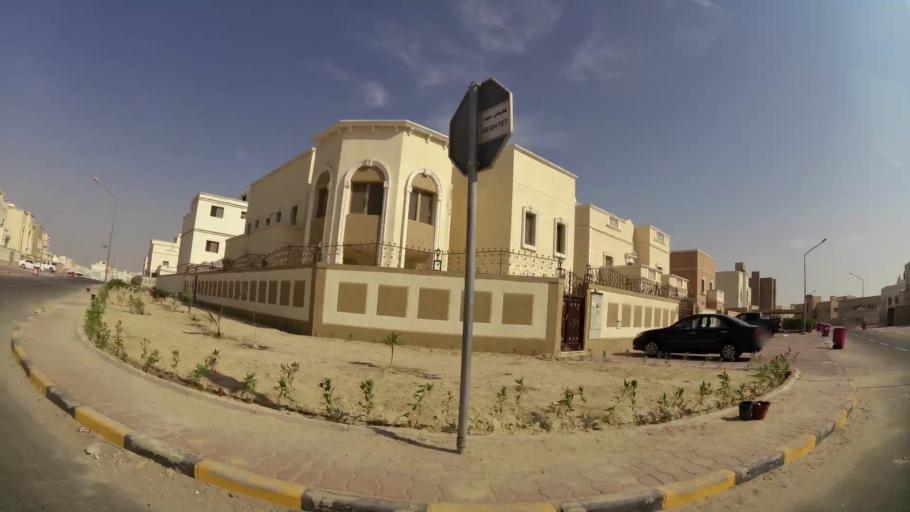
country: KW
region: Al Ahmadi
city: Al Wafrah
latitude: 28.7914
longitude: 48.0698
